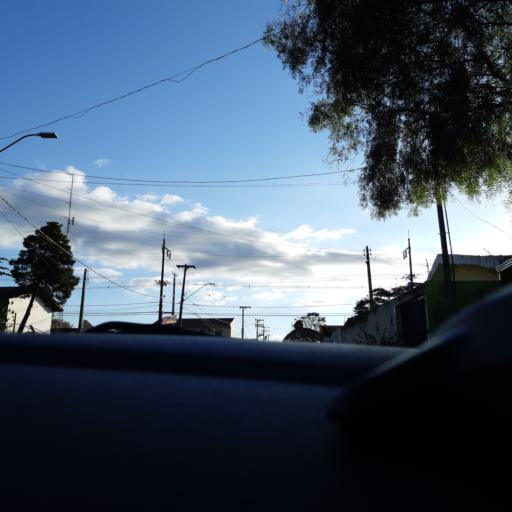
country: BR
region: Sao Paulo
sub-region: Ourinhos
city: Ourinhos
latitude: -22.9853
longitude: -49.8595
